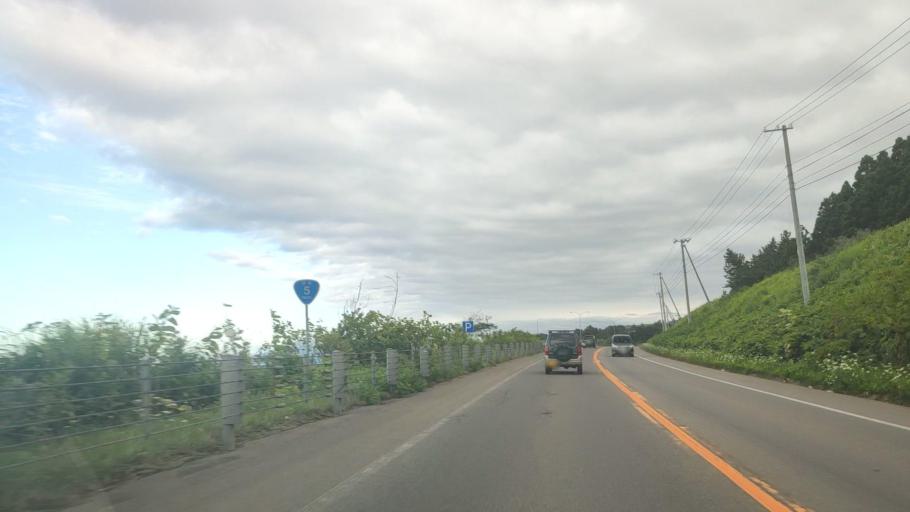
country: JP
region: Hokkaido
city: Nanae
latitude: 42.2063
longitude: 140.4045
